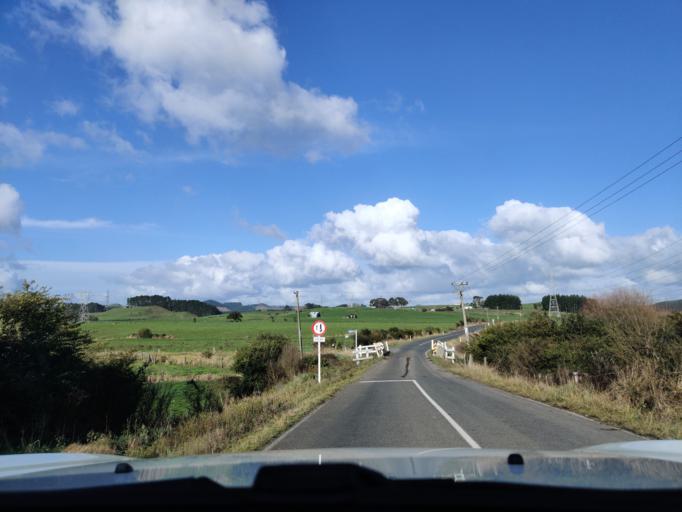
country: NZ
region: Waikato
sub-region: Waikato District
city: Te Kauwhata
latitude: -37.2621
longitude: 175.1947
